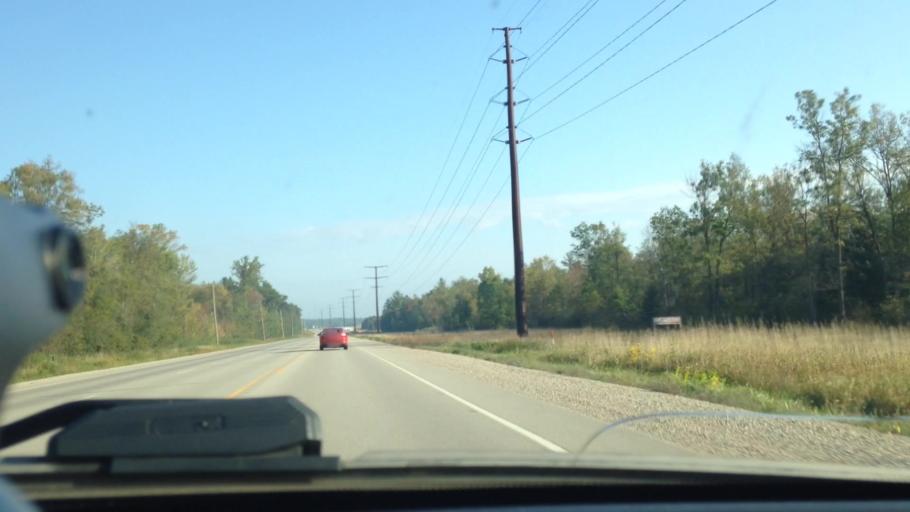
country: US
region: Wisconsin
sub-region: Marinette County
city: Peshtigo
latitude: 45.1901
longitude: -87.9950
